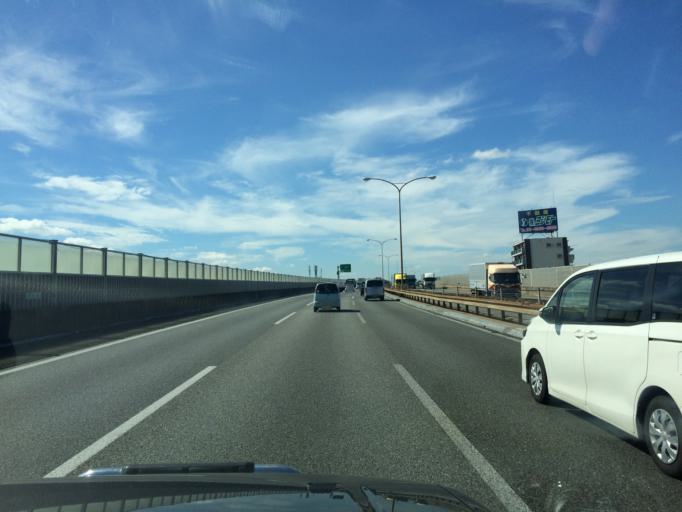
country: JP
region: Osaka
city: Yao
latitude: 34.6382
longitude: 135.5921
